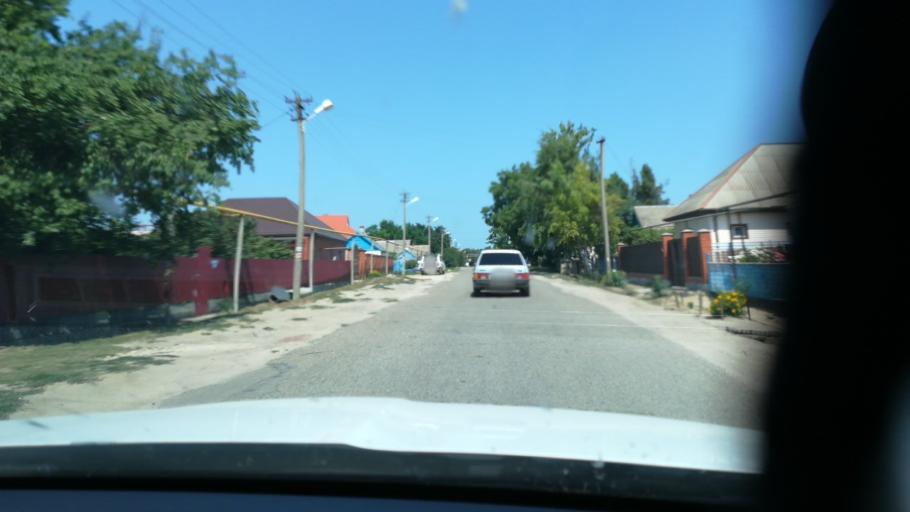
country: RU
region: Krasnodarskiy
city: Starotitarovskaya
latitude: 45.2142
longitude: 37.1435
